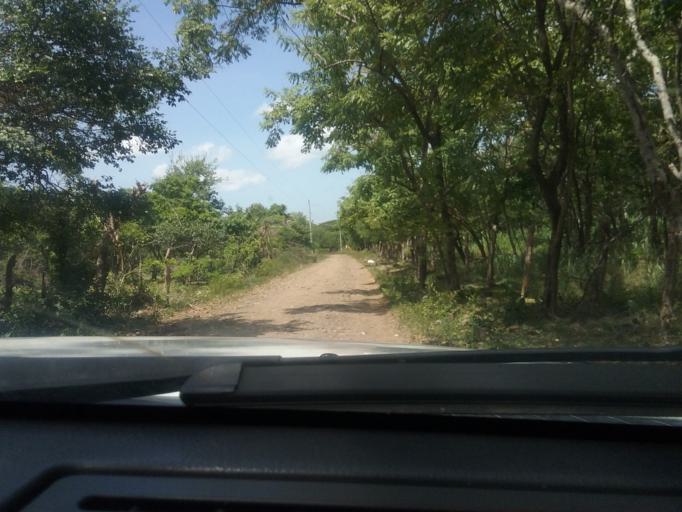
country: NI
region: Matagalpa
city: Terrabona
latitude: 12.6533
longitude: -85.9935
